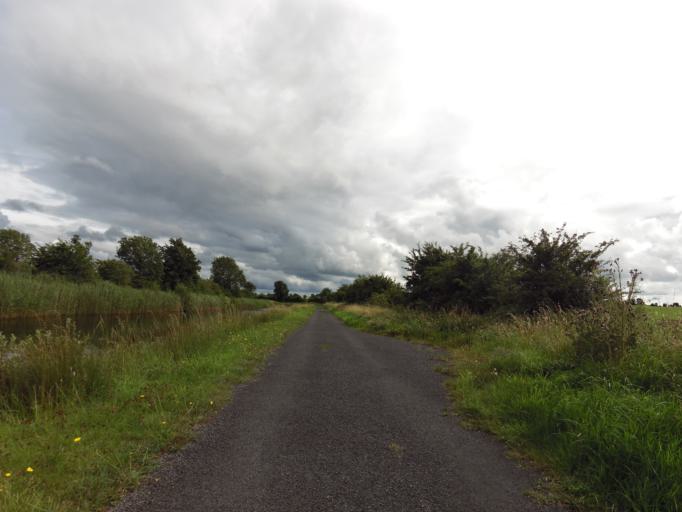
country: IE
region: Leinster
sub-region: An Iarmhi
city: An Muileann gCearr
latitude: 53.5600
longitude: -7.5027
